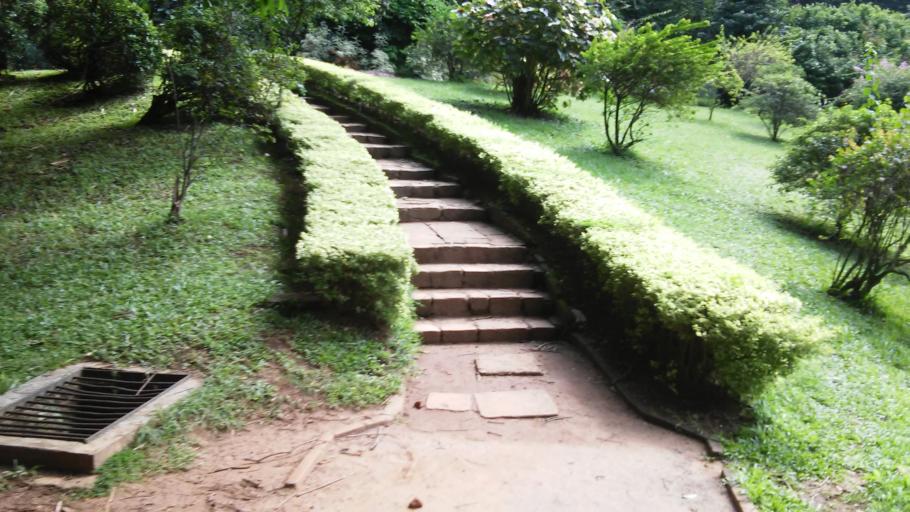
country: LK
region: Central
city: Kandy
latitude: 7.2677
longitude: 80.5940
